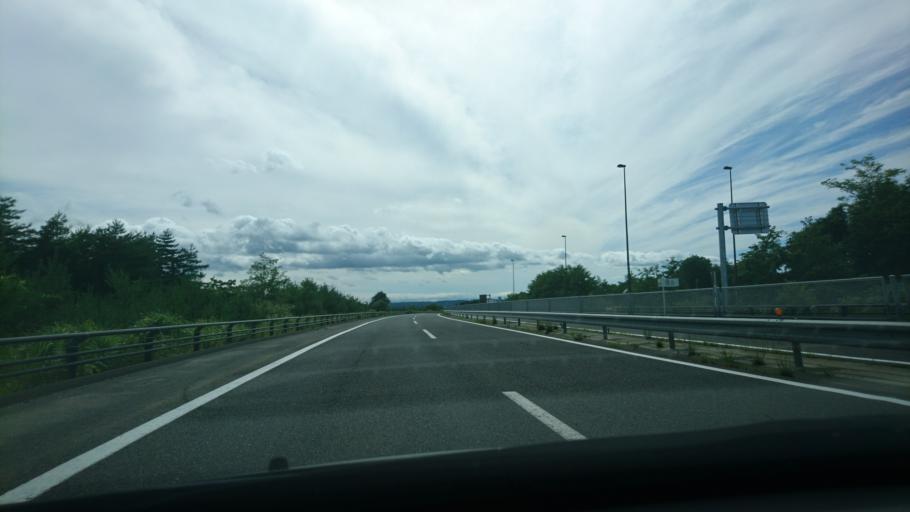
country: JP
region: Aomori
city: Hachinohe
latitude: 40.4800
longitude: 141.5532
